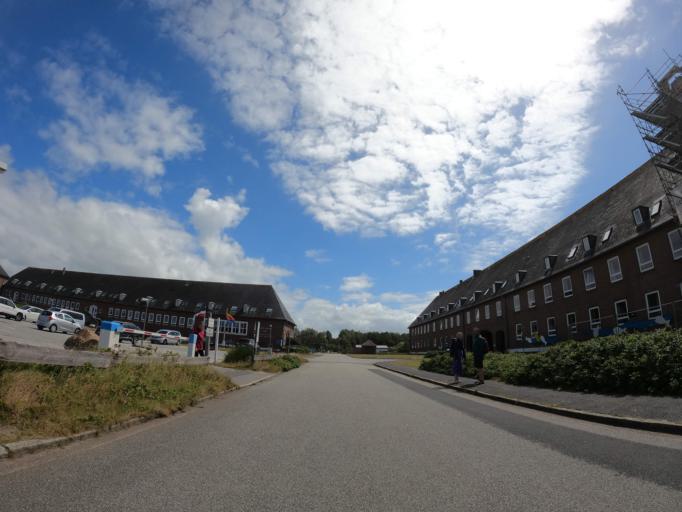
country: DE
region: Schleswig-Holstein
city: Westerland
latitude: 54.8570
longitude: 8.2959
